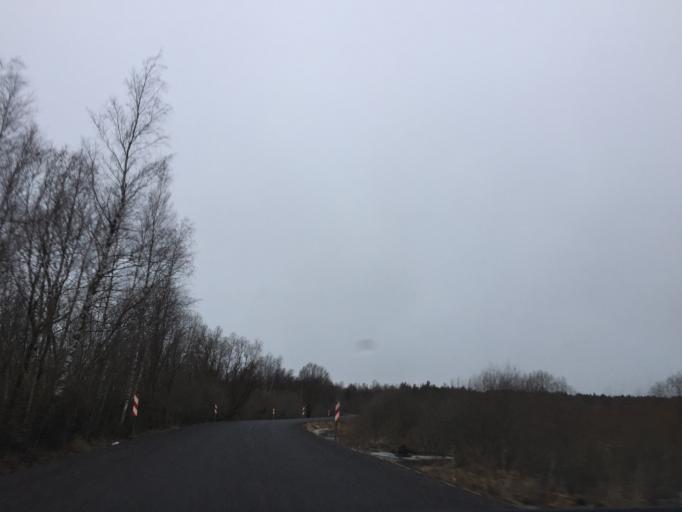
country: EE
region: Laeaene
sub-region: Lihula vald
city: Lihula
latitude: 58.6608
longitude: 23.5755
